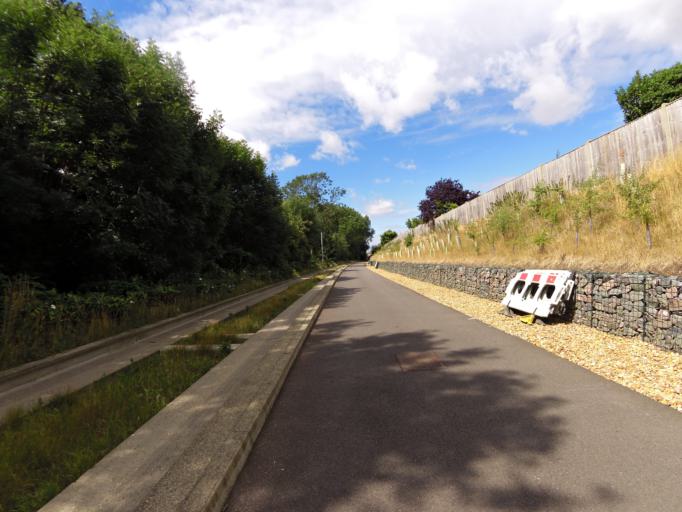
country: GB
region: England
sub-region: Cambridgeshire
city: Grantchester
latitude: 52.1691
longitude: 0.1144
